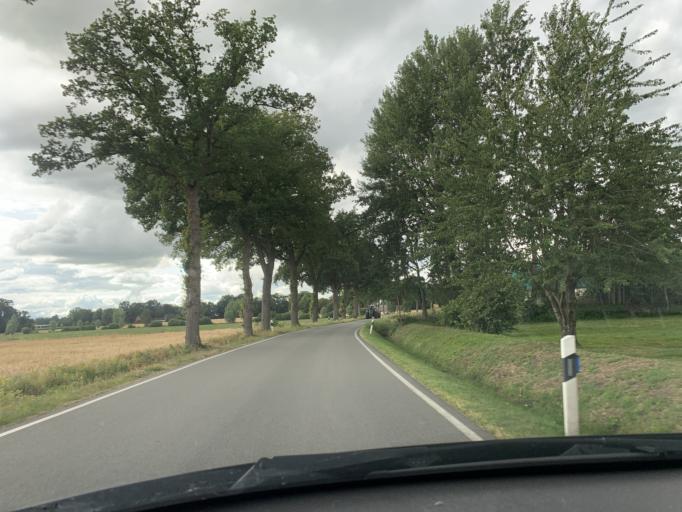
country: DE
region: Lower Saxony
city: Westerstede
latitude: 53.2226
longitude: 7.9046
